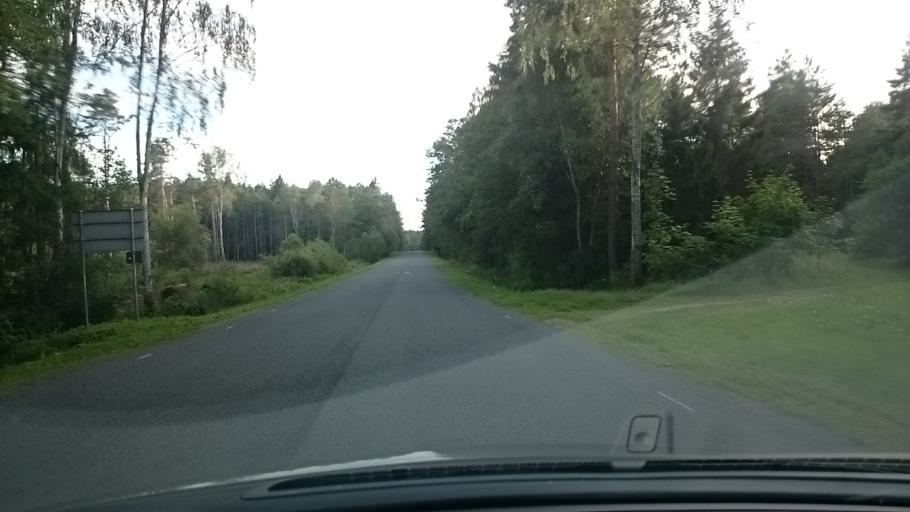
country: EE
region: Saare
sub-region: Kuressaare linn
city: Kuressaare
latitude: 58.4466
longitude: 22.2423
